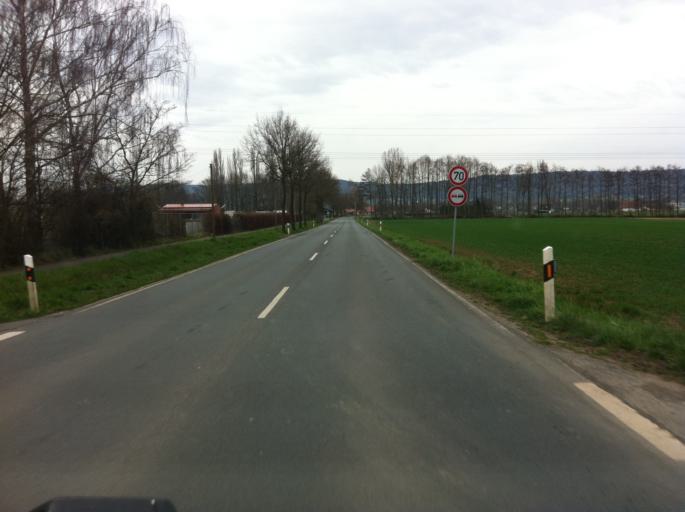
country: DE
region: North Rhine-Westphalia
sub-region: Regierungsbezirk Detmold
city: Minden
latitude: 52.2866
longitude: 8.8640
